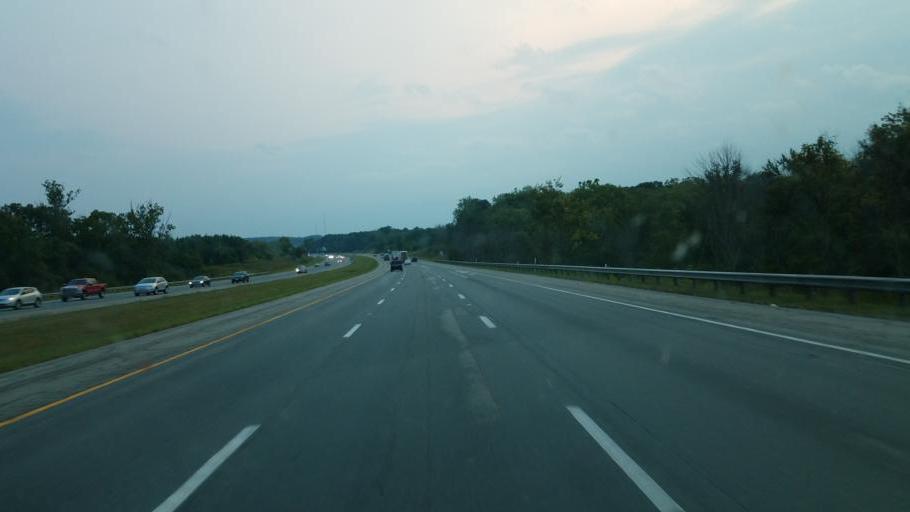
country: US
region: Ohio
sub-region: Wayne County
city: West Salem
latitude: 40.9330
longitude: -82.1149
